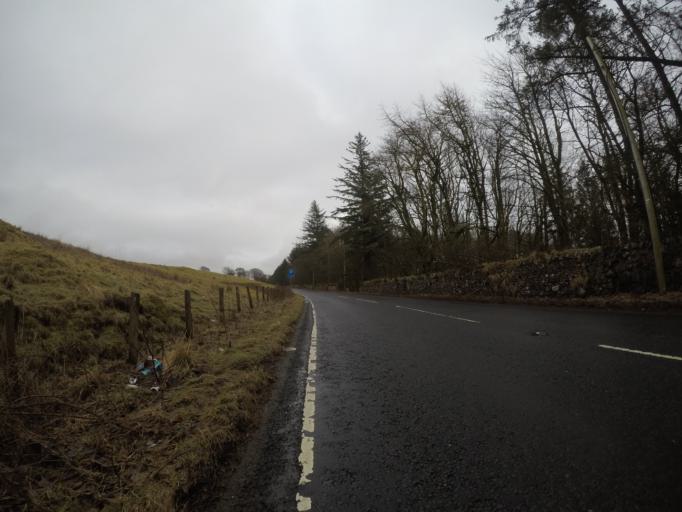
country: GB
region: Scotland
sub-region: North Ayrshire
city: Fairlie
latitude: 55.7750
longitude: -4.8340
